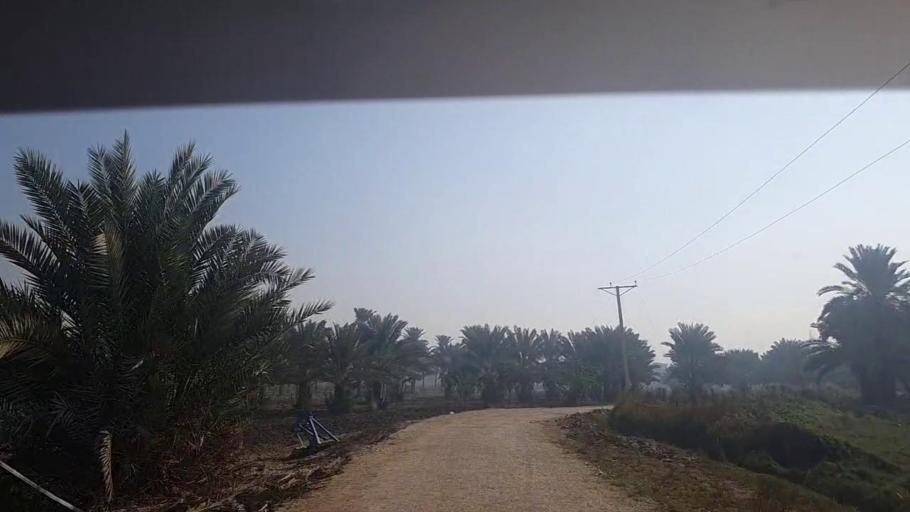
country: PK
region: Sindh
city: Khairpur
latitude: 27.4779
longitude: 68.7213
